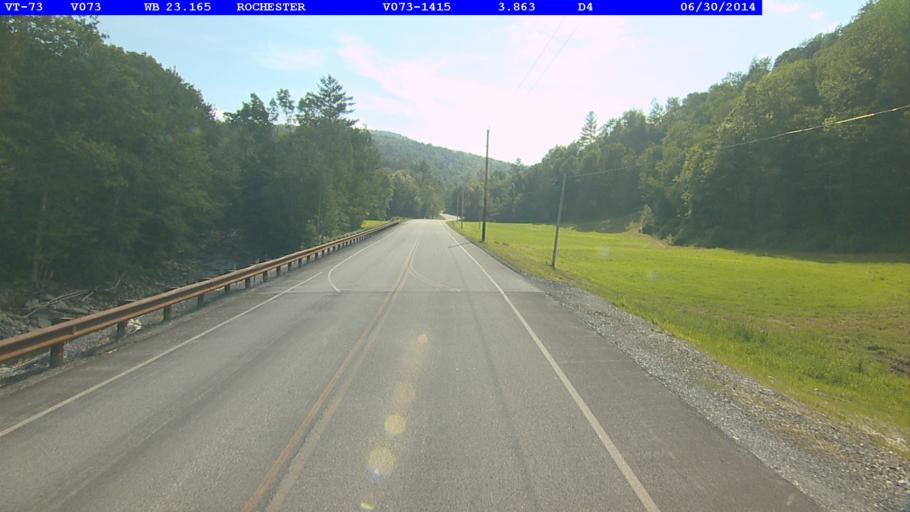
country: US
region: Vermont
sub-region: Rutland County
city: Brandon
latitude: 43.8536
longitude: -72.8941
